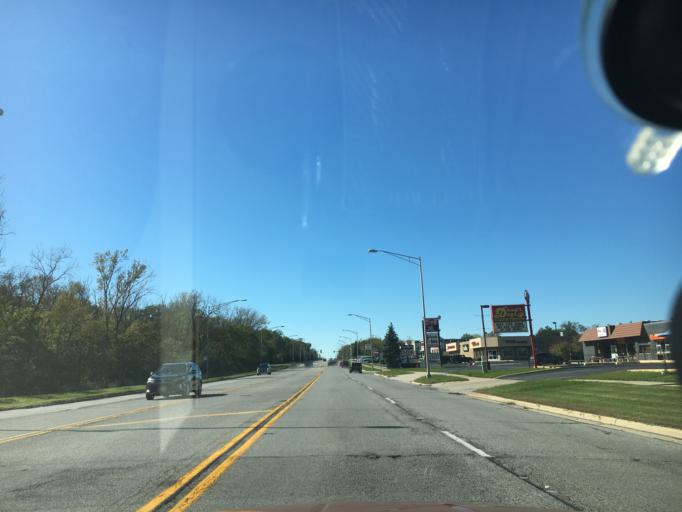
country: US
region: Illinois
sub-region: Cook County
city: Oak Forest
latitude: 41.6027
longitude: -87.7706
